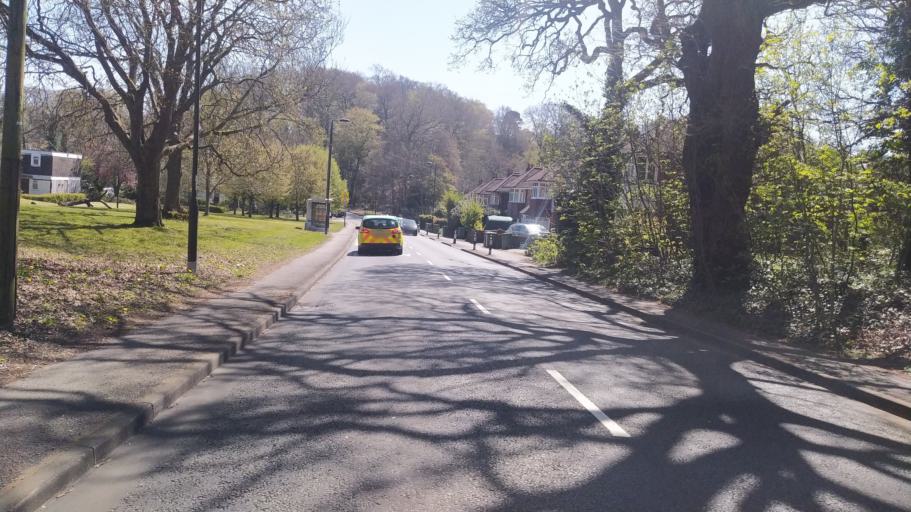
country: GB
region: England
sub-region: Southampton
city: Southampton
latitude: 50.9381
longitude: -1.4252
